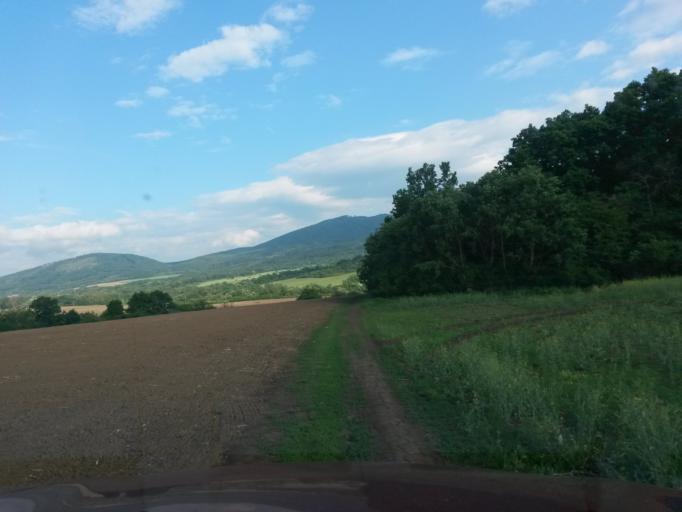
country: SK
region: Kosicky
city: Secovce
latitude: 48.7437
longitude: 21.4667
